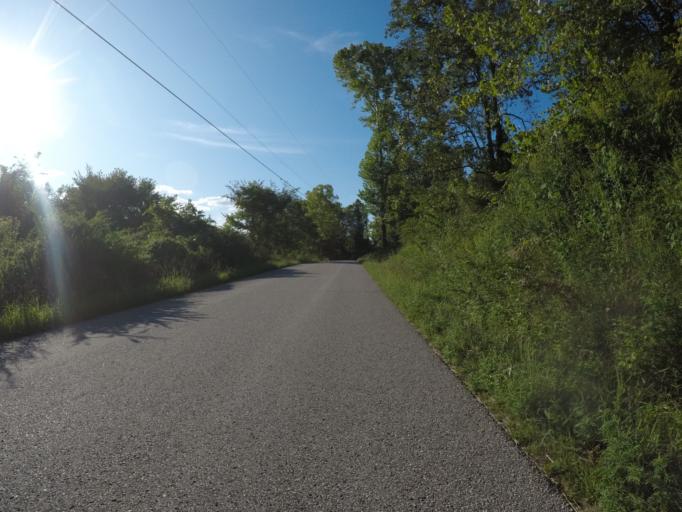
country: US
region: West Virginia
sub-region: Cabell County
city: Huntington
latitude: 38.5136
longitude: -82.4983
